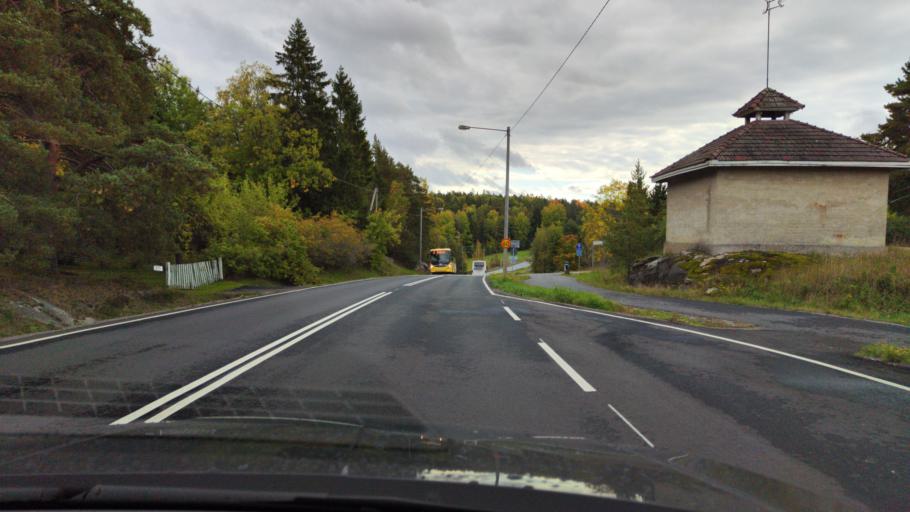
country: FI
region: Varsinais-Suomi
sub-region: Turku
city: Raisio
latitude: 60.3668
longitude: 22.1760
